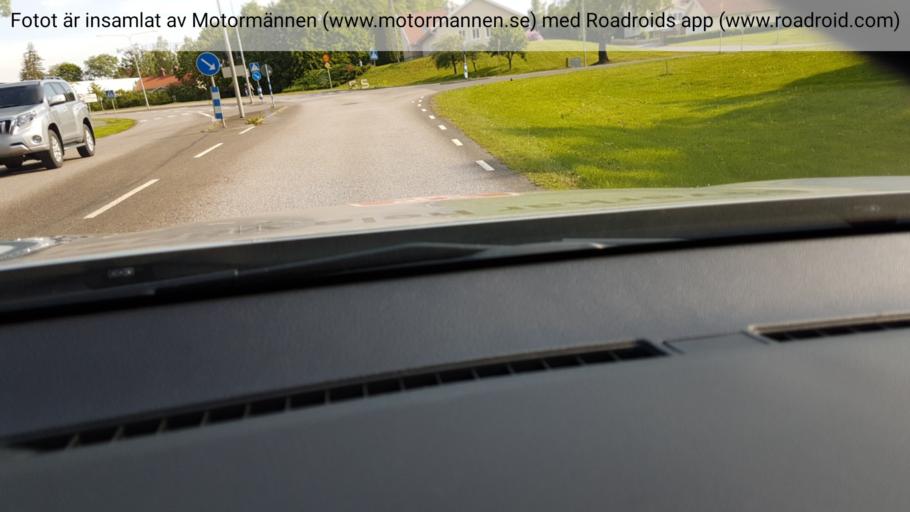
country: SE
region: Vaestra Goetaland
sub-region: Skovde Kommun
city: Skoevde
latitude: 58.3850
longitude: 13.8604
